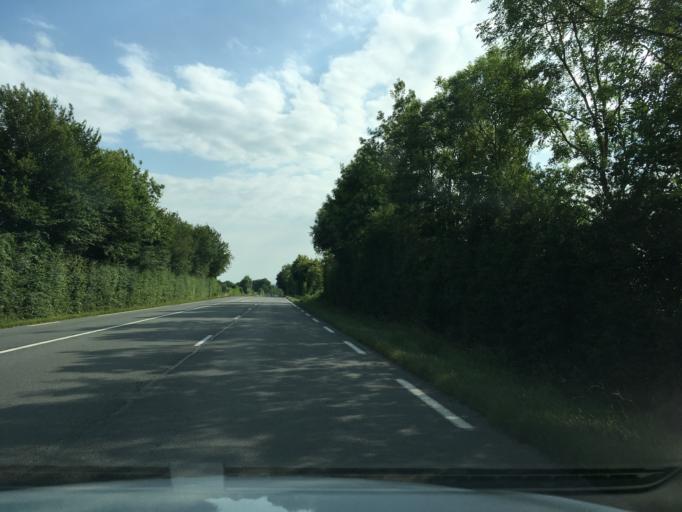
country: FR
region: Poitou-Charentes
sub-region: Departement des Deux-Sevres
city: Champdeniers-Saint-Denis
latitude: 46.4978
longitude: -0.3426
